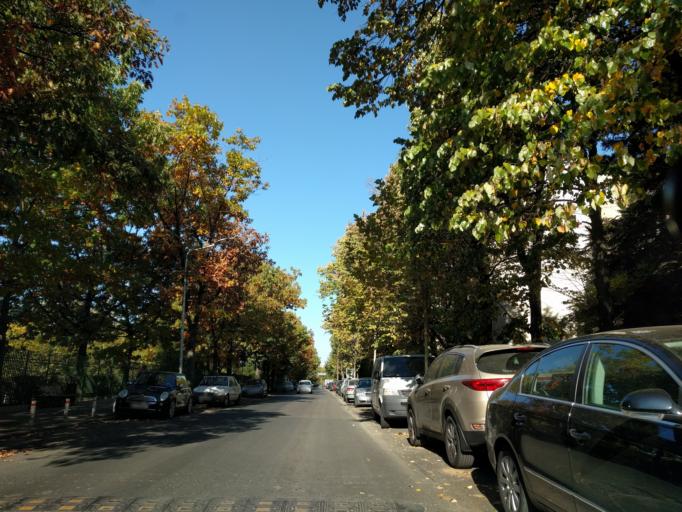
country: RO
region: Ilfov
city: Dobroesti
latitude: 44.4220
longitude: 26.1595
